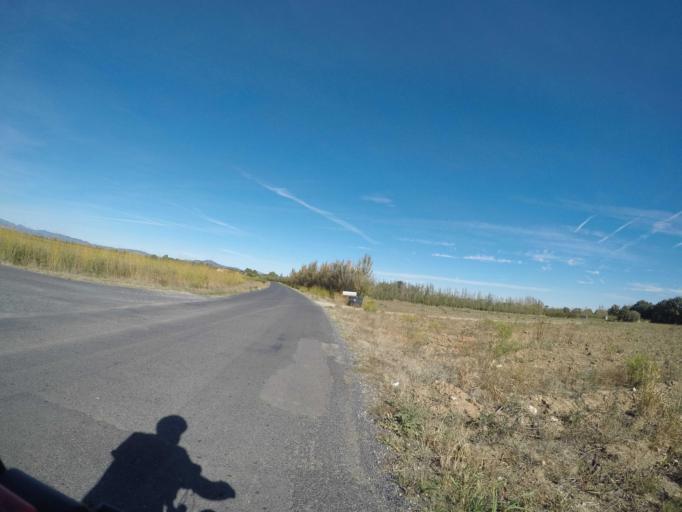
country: FR
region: Languedoc-Roussillon
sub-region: Departement des Pyrenees-Orientales
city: Ponteilla
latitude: 42.6456
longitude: 2.8019
